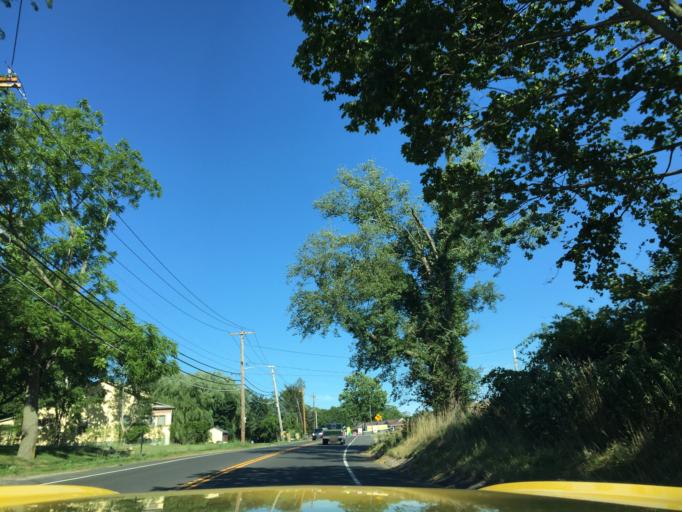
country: US
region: New York
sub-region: Suffolk County
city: Aquebogue
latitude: 40.9480
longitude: -72.6145
